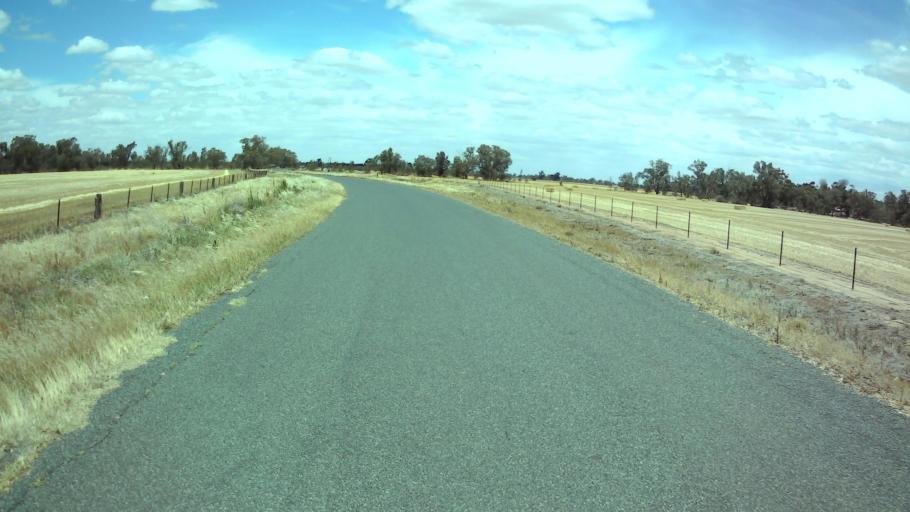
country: AU
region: New South Wales
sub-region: Weddin
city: Grenfell
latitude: -34.0352
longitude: 147.7896
